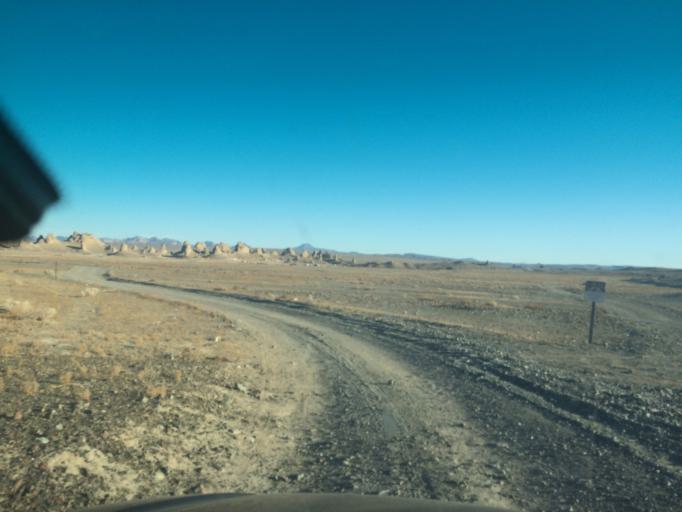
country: US
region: California
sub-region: San Bernardino County
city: Searles Valley
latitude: 35.6256
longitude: -117.3794
